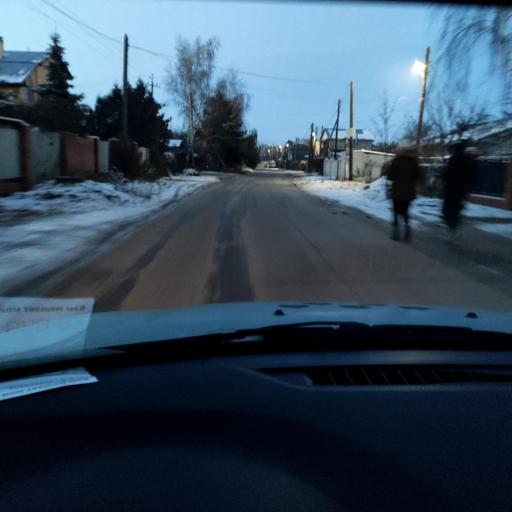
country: RU
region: Samara
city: Tol'yatti
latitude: 53.5614
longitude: 49.3889
